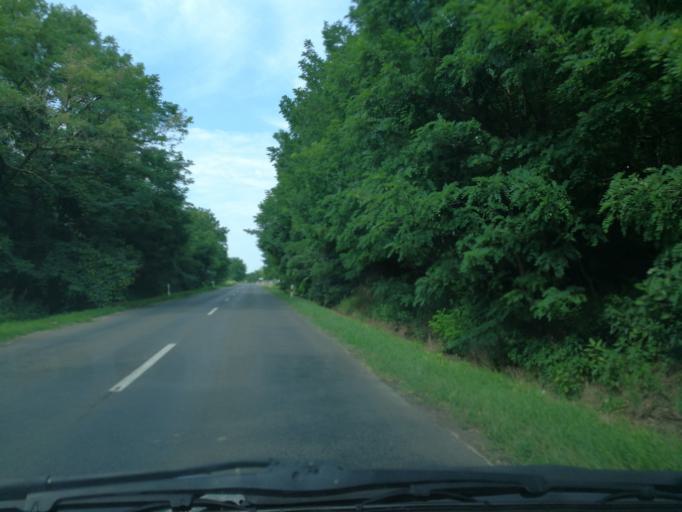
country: HU
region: Bacs-Kiskun
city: Davod
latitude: 46.0046
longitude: 18.9303
